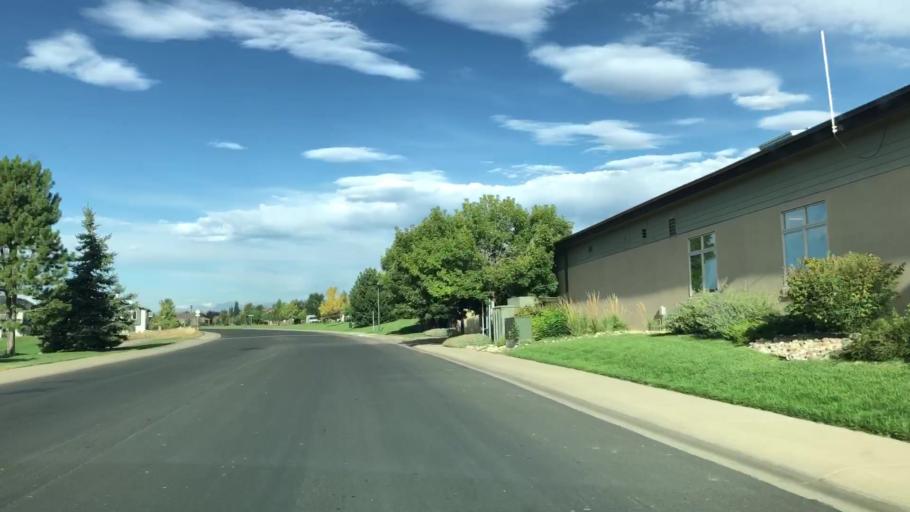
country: US
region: Colorado
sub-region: Weld County
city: Windsor
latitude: 40.4615
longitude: -104.9712
